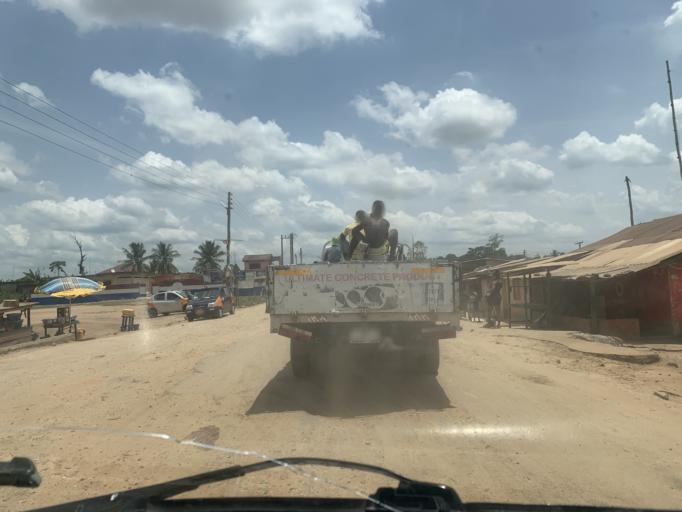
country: GH
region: Central
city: Swedru
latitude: 5.5106
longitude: -0.6942
